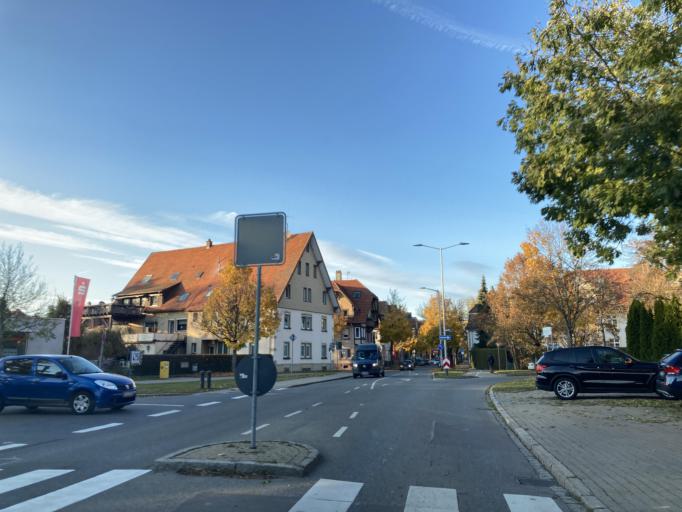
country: DE
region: Baden-Wuerttemberg
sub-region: Freiburg Region
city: Villingen-Schwenningen
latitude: 48.0509
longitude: 8.4615
